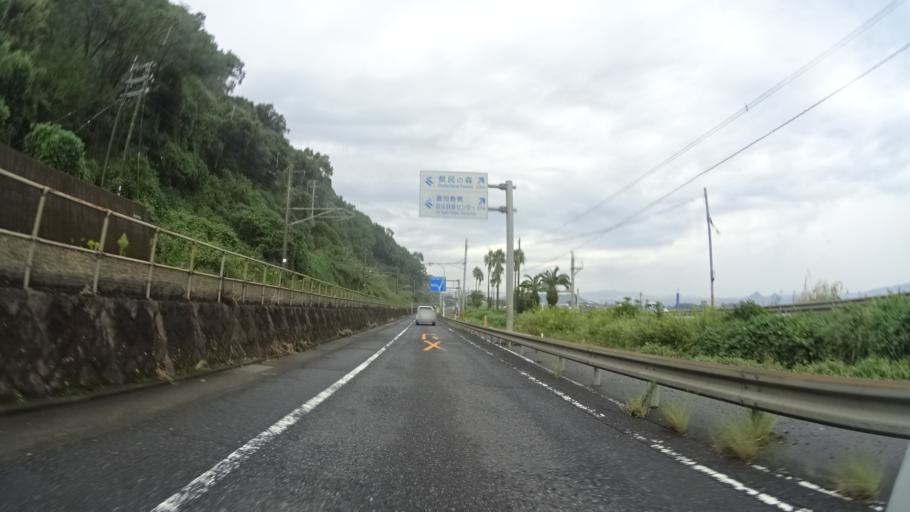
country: JP
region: Kagoshima
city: Kajiki
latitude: 31.6934
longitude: 130.6147
